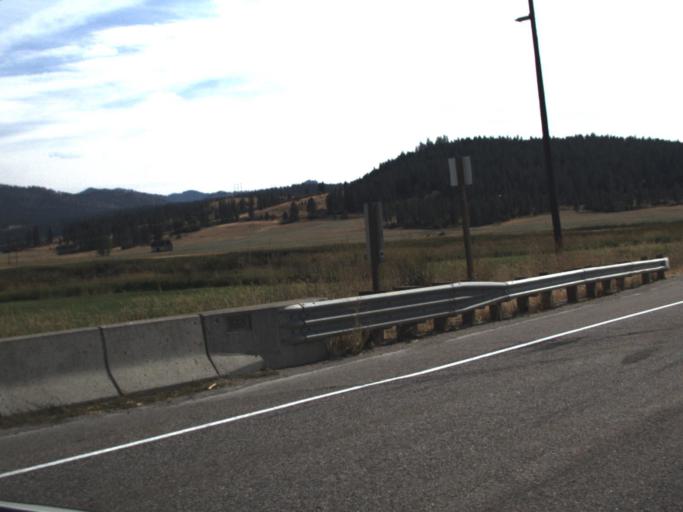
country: US
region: Washington
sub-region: Stevens County
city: Chewelah
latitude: 48.2208
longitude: -117.7154
